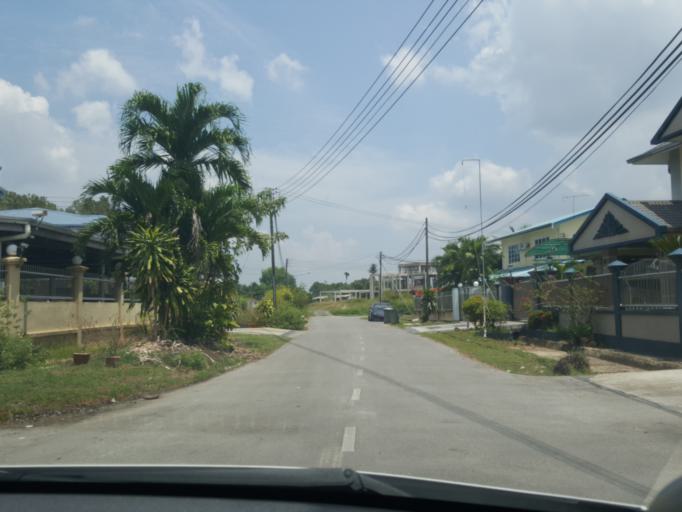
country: MY
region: Sarawak
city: Sarikei
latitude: 2.1210
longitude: 111.5259
